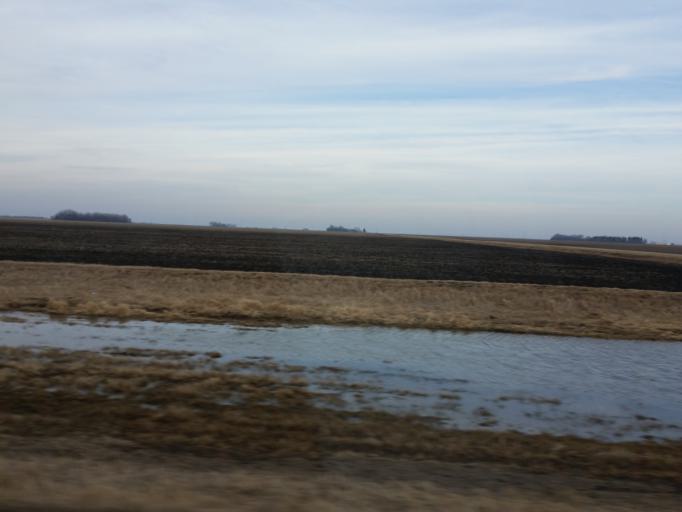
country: US
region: North Dakota
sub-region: Cass County
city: Casselton
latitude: 46.9635
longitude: -97.2195
